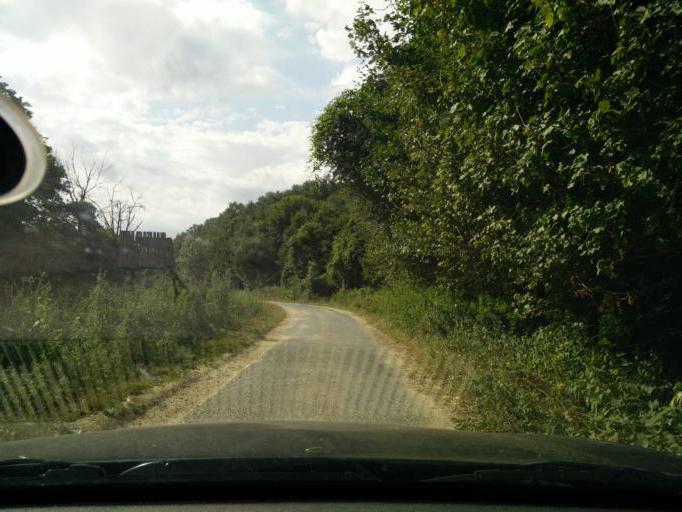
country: HU
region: Komarom-Esztergom
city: Sutto
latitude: 47.7147
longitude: 18.4557
